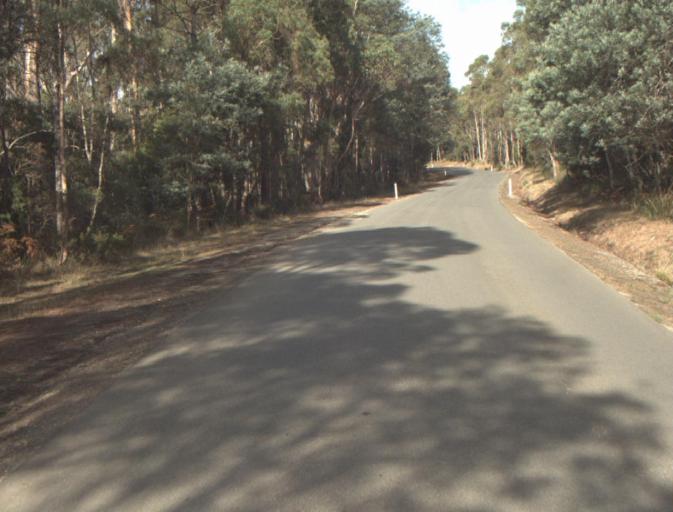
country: AU
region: Tasmania
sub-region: Launceston
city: Mayfield
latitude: -41.2378
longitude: 147.1886
